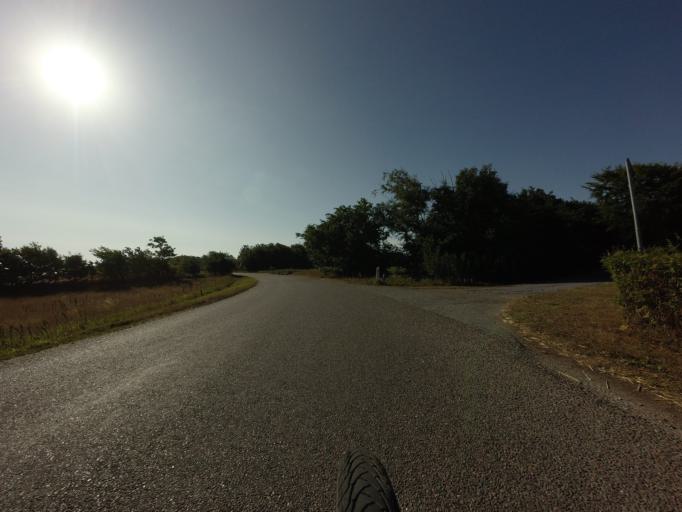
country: DK
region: North Denmark
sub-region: Hjorring Kommune
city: Vra
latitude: 57.3822
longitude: 9.9967
